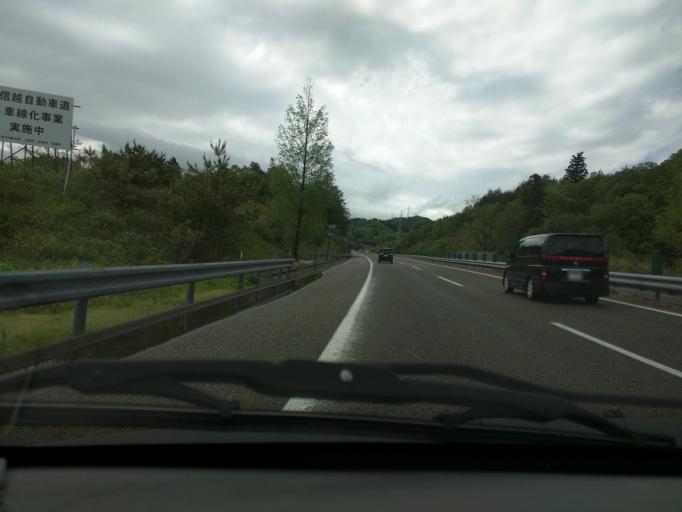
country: JP
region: Niigata
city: Joetsu
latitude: 37.1356
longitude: 138.2136
